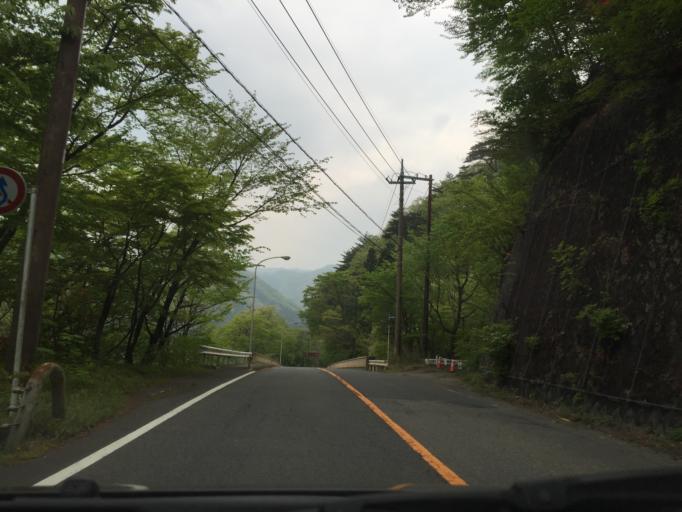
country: JP
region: Tochigi
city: Nikko
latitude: 36.8665
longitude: 139.7121
